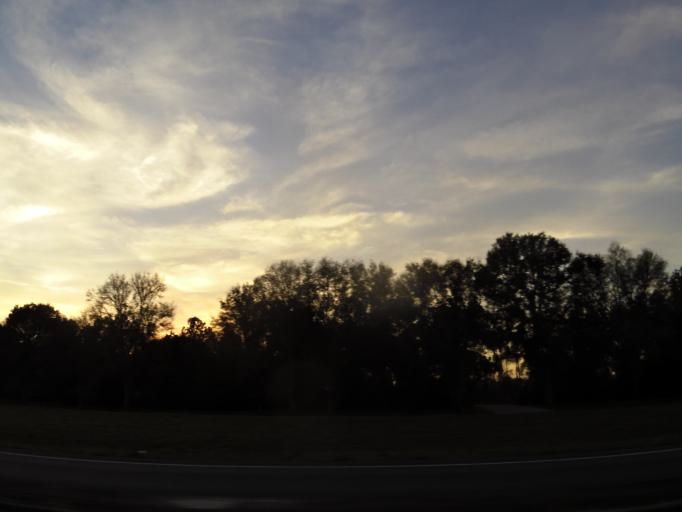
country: US
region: Florida
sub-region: Volusia County
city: North DeLand
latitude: 29.1027
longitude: -81.2951
